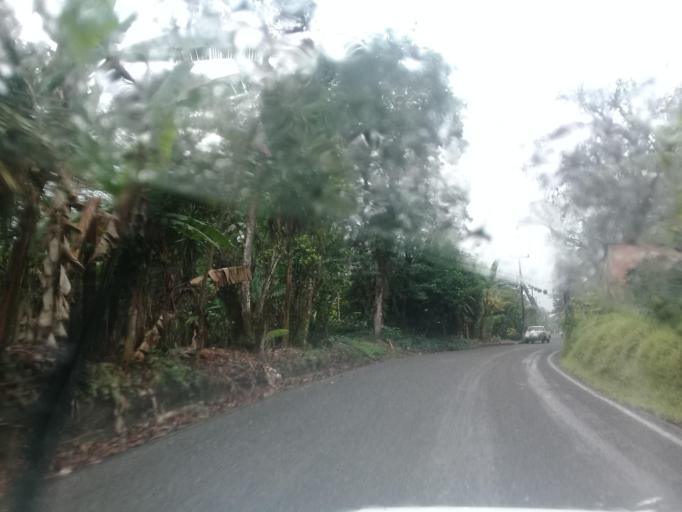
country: MX
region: Veracruz
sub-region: Amatlan de los Reyes
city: Centro de Readaptacion Social
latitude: 18.7996
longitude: -96.9423
